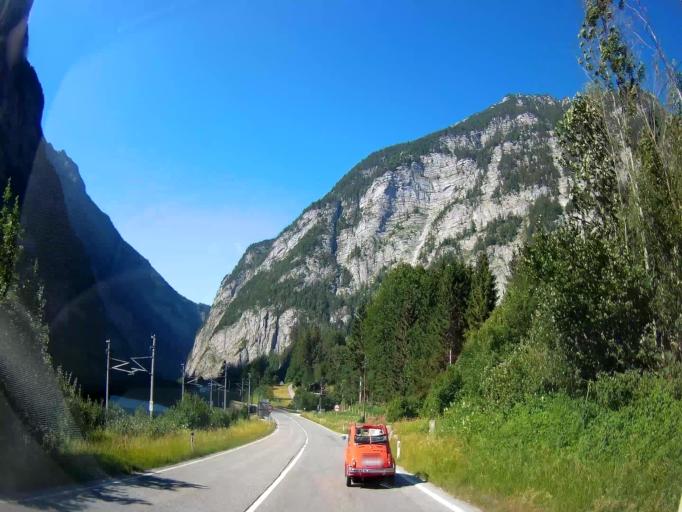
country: AT
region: Salzburg
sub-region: Politischer Bezirk Hallein
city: Golling an der Salzach
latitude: 47.5406
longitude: 13.1712
